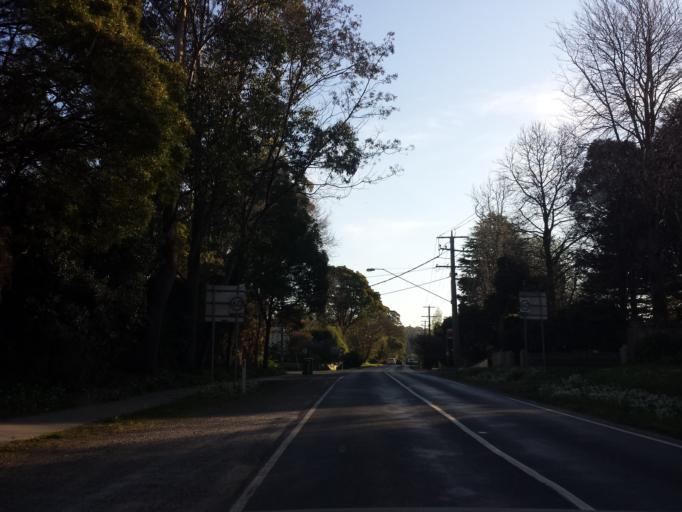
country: AU
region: Victoria
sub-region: Yarra Ranges
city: Ferny Creek
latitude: -37.8698
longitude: 145.3481
